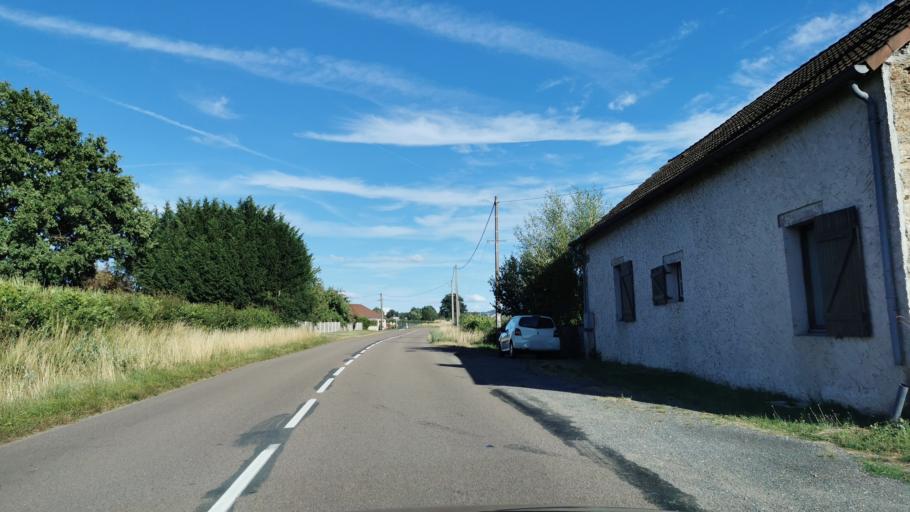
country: FR
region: Bourgogne
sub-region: Departement de Saone-et-Loire
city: Marmagne
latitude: 46.8560
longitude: 4.3152
